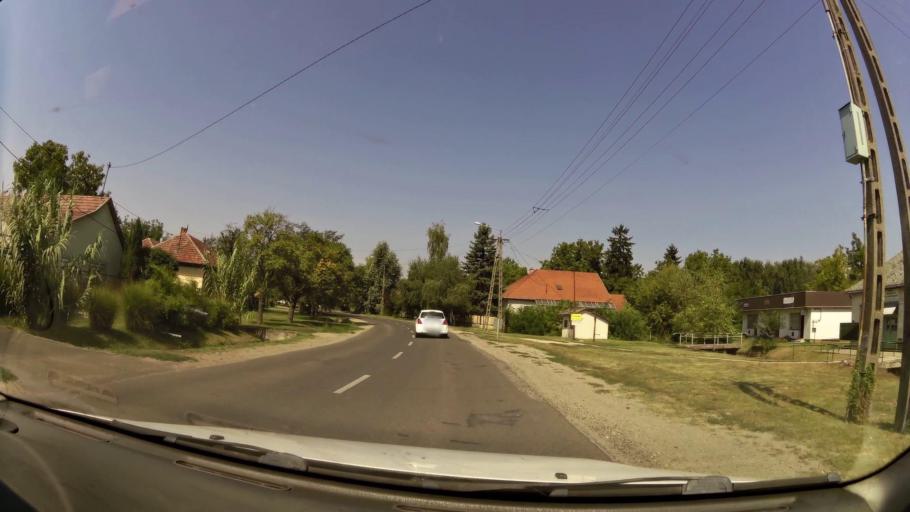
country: HU
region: Pest
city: Tapiobicske
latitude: 47.3593
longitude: 19.6920
